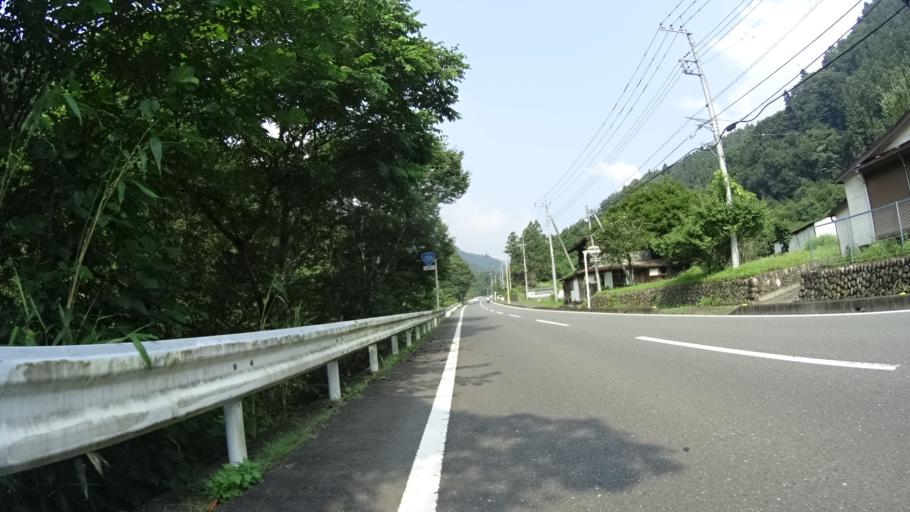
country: JP
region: Saitama
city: Chichibu
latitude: 36.0349
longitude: 138.9237
